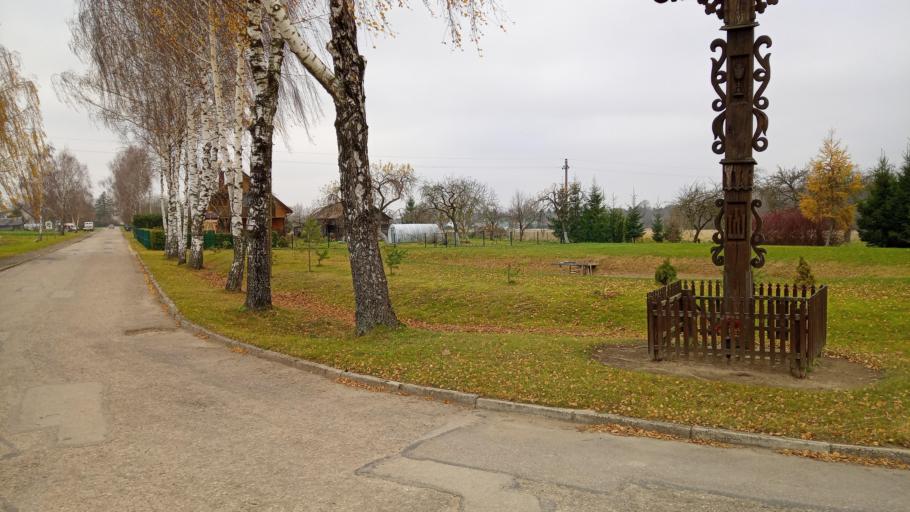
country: LT
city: Sakiai
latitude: 55.0762
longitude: 23.1739
